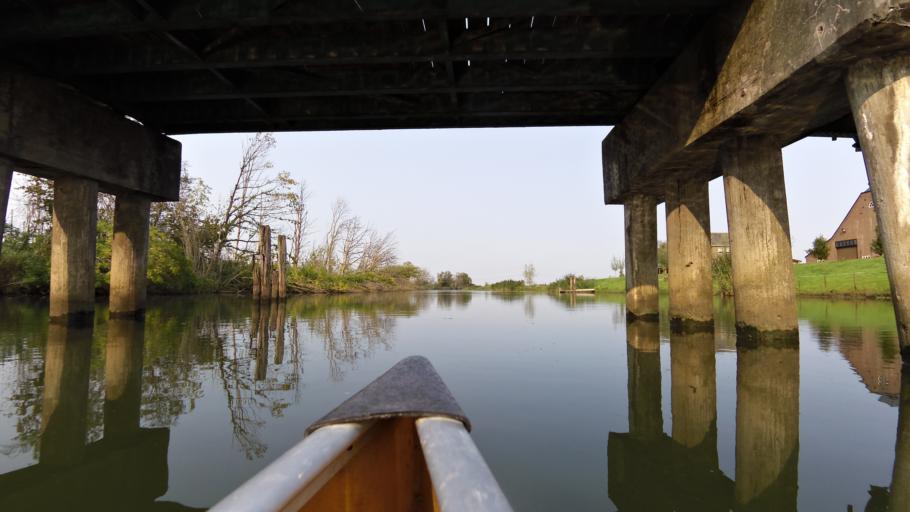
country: NL
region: South Holland
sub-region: Gemeente Sliedrecht
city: Sliedrecht
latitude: 51.7811
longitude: 4.8063
